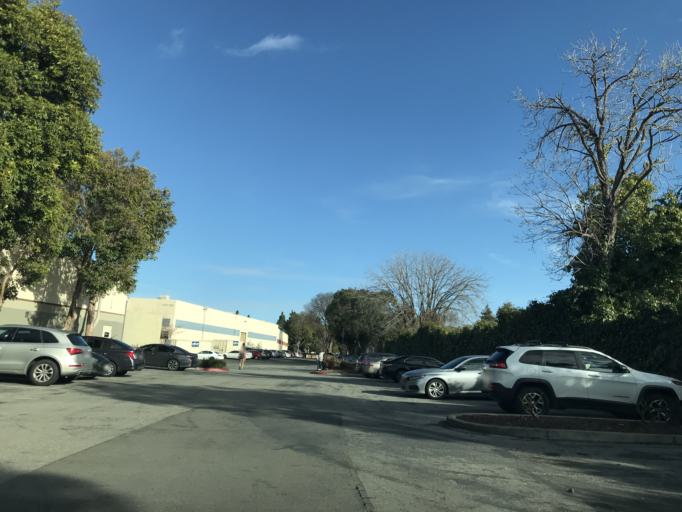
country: US
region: California
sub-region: San Mateo County
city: East Palo Alto
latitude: 37.4764
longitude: -122.1489
